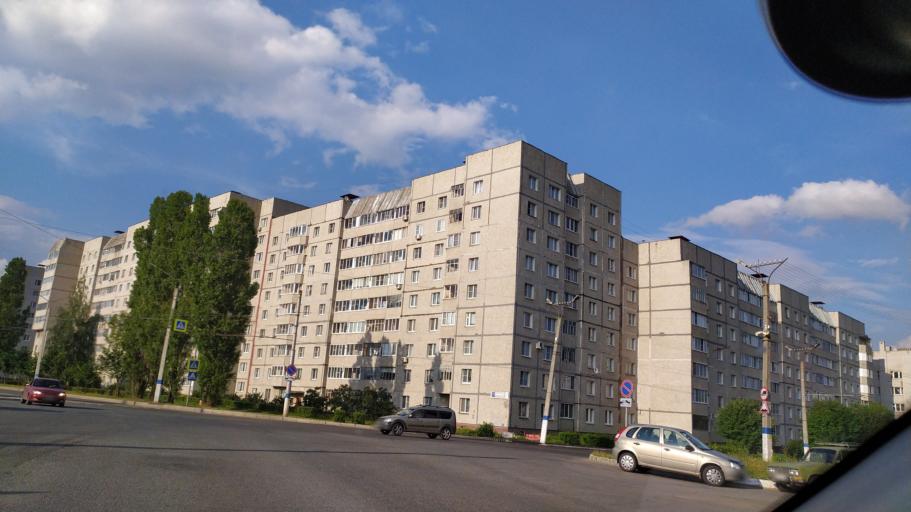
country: RU
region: Chuvashia
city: Novocheboksarsk
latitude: 56.1170
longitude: 47.4442
